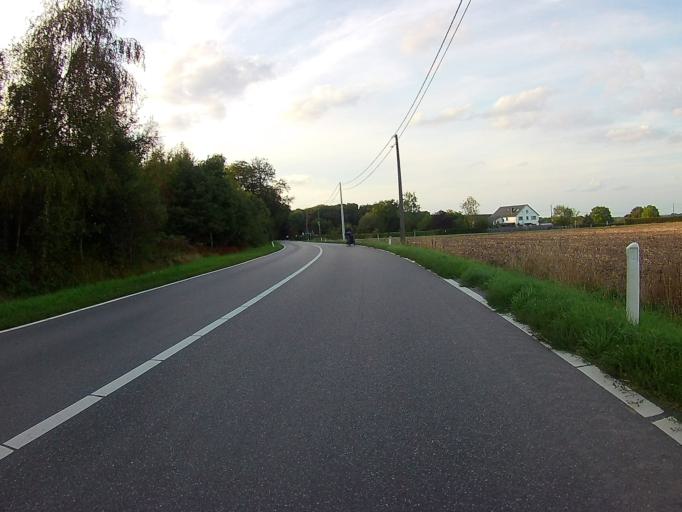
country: BE
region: Wallonia
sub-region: Province de Liege
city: Aubel
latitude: 50.7346
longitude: 5.8634
